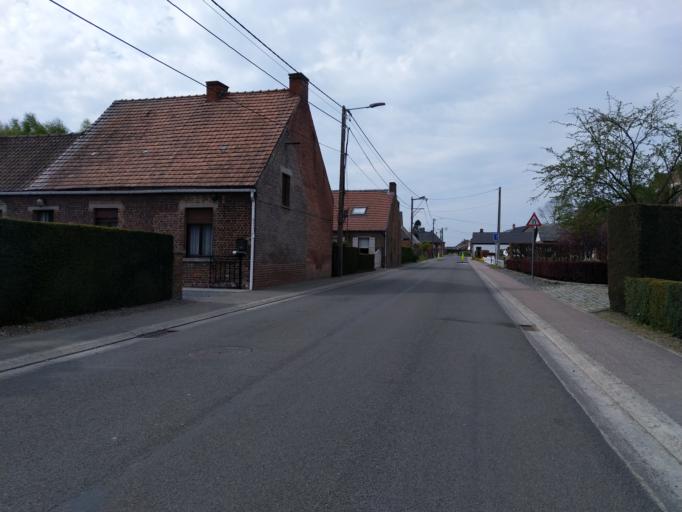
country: BE
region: Wallonia
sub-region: Province du Hainaut
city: Jurbise
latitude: 50.5084
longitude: 3.8799
